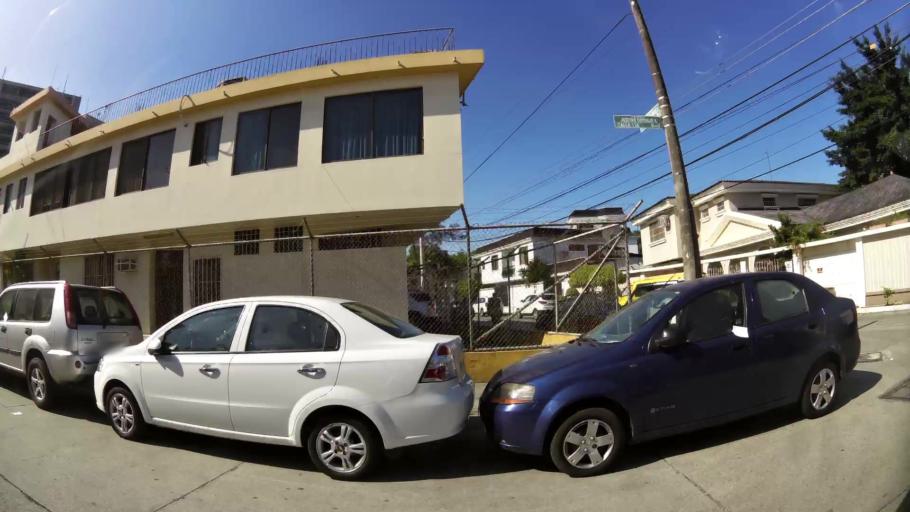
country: EC
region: Guayas
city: Guayaquil
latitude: -2.1634
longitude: -79.8992
